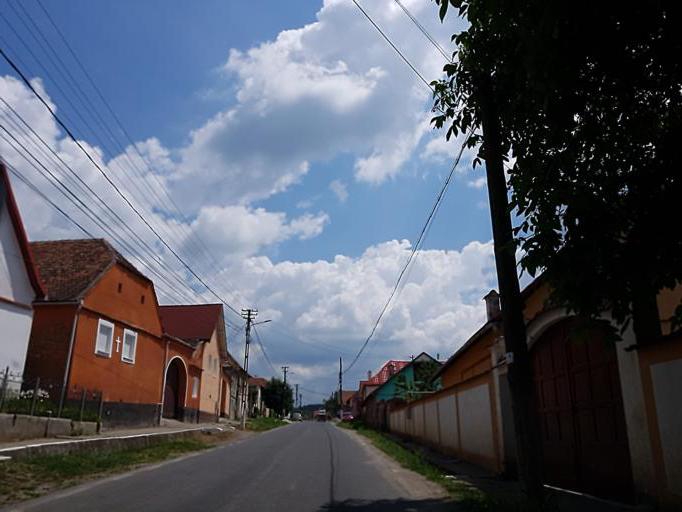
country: RO
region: Sibiu
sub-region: Comuna Seica Mica
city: Seica Mica
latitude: 46.0547
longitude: 24.1303
